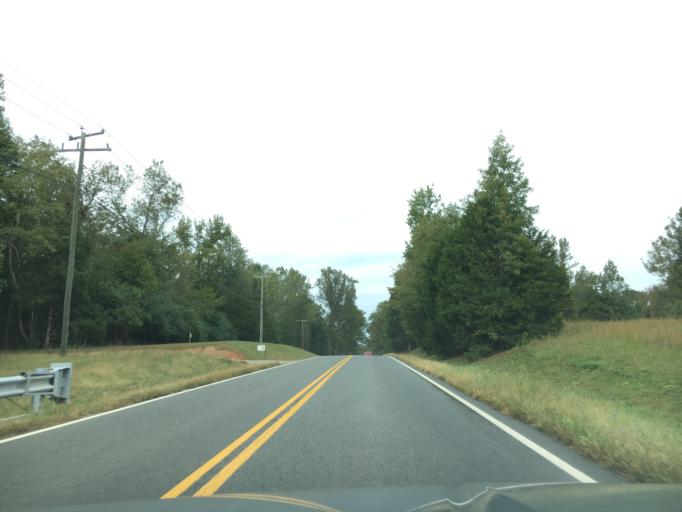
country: US
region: Virginia
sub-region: Goochland County
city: Goochland
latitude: 37.7335
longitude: -77.8389
